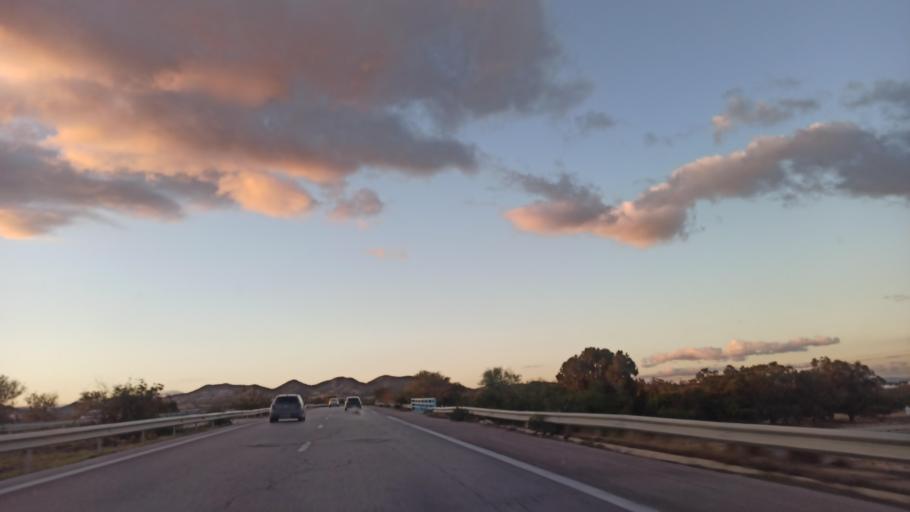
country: TN
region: Susah
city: Harqalah
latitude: 36.2129
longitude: 10.4236
